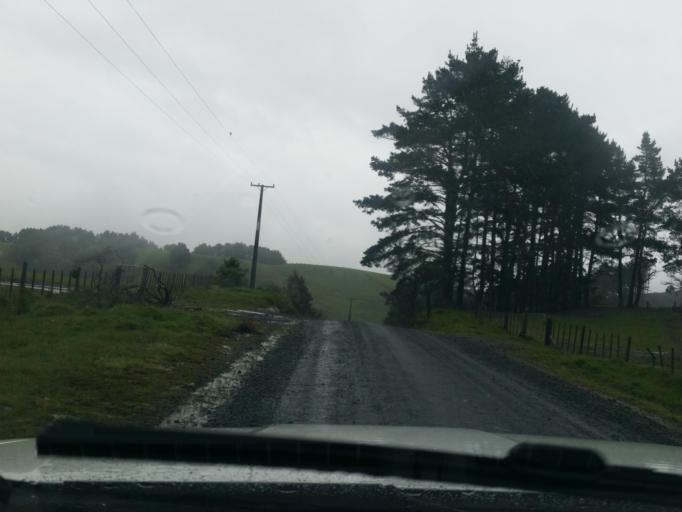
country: NZ
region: Northland
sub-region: Whangarei
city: Maungatapere
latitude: -35.8047
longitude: 174.0478
